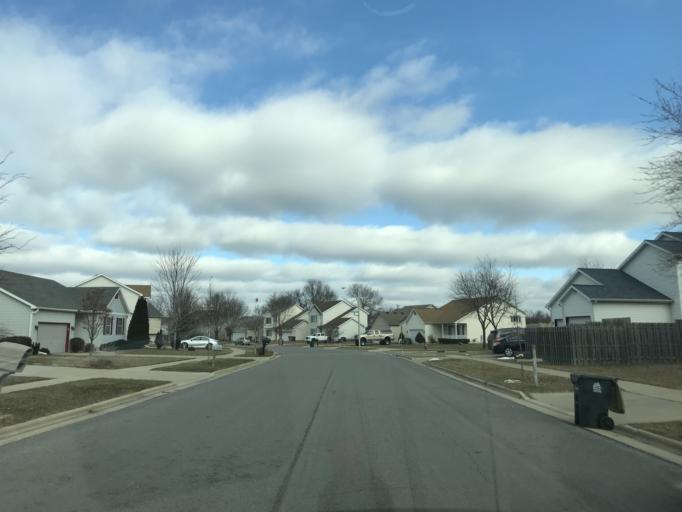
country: US
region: Wisconsin
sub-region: Dane County
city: Monona
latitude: 43.1151
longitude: -89.2898
